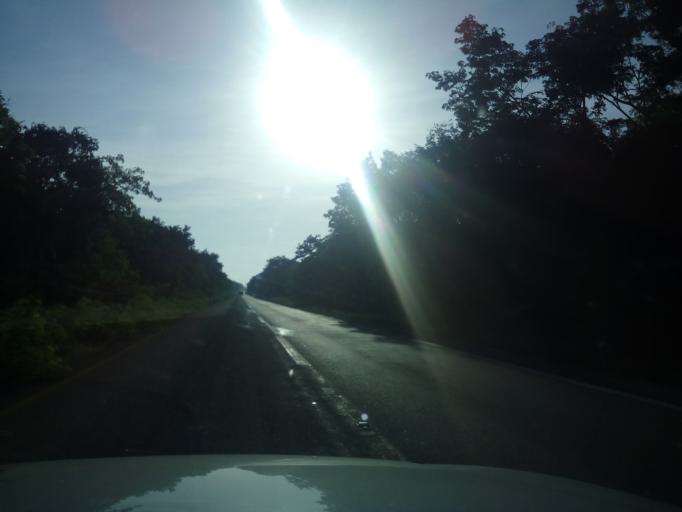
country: MX
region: Yucatan
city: Piste
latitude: 20.7350
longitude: -88.6112
